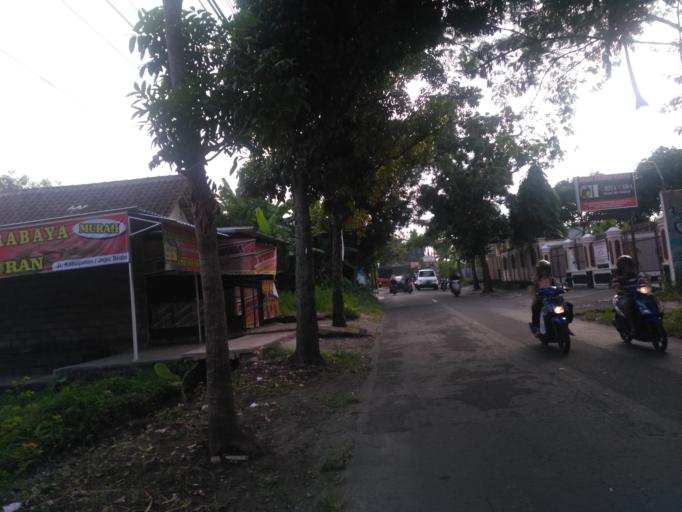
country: ID
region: Daerah Istimewa Yogyakarta
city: Yogyakarta
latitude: -7.7646
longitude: 110.3446
